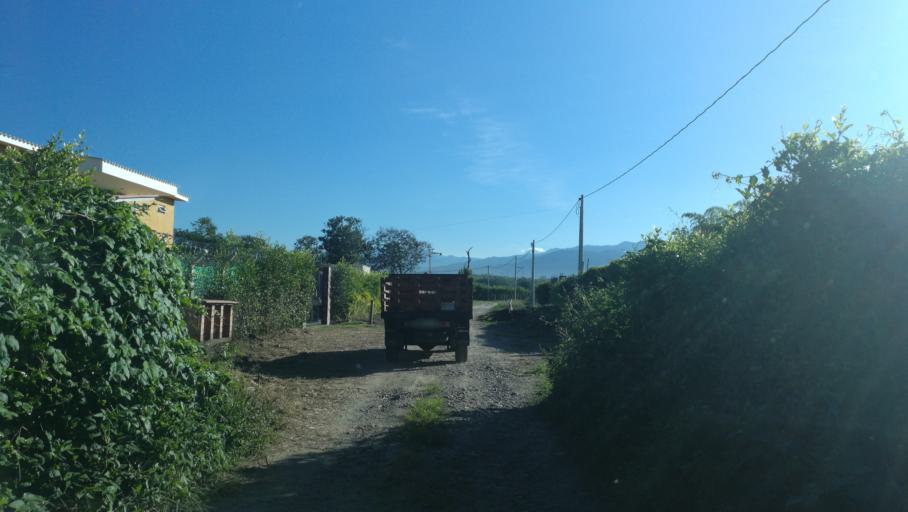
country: CO
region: Quindio
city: Armenia
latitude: 4.5135
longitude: -75.7198
